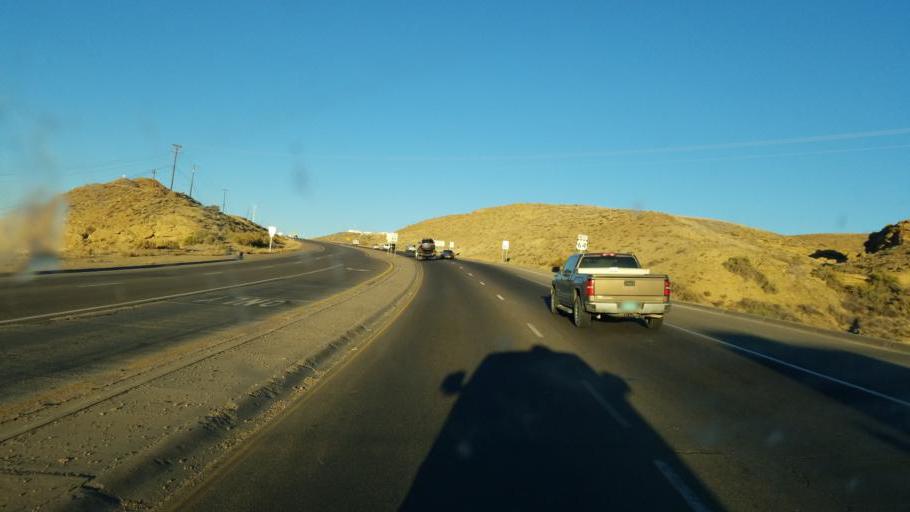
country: US
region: New Mexico
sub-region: San Juan County
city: Farmington
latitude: 36.7380
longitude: -108.2525
